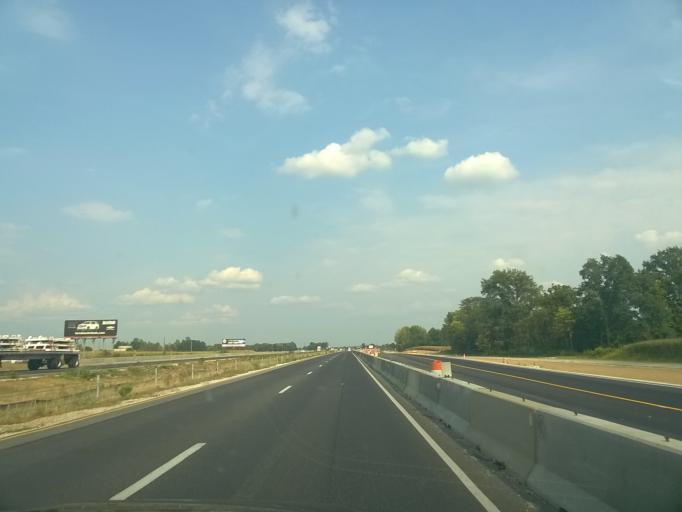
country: US
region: Indiana
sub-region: Vigo County
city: Terre Haute
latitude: 39.4306
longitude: -87.3422
